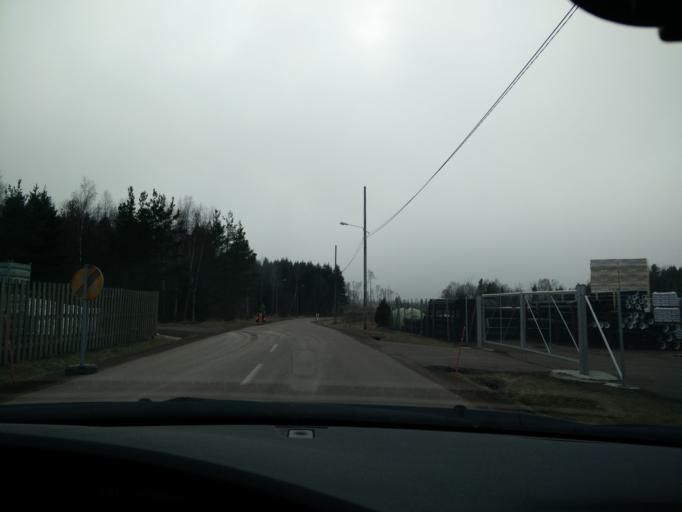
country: AX
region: Mariehamns stad
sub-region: Mariehamn
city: Mariehamn
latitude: 60.1088
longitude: 19.9118
